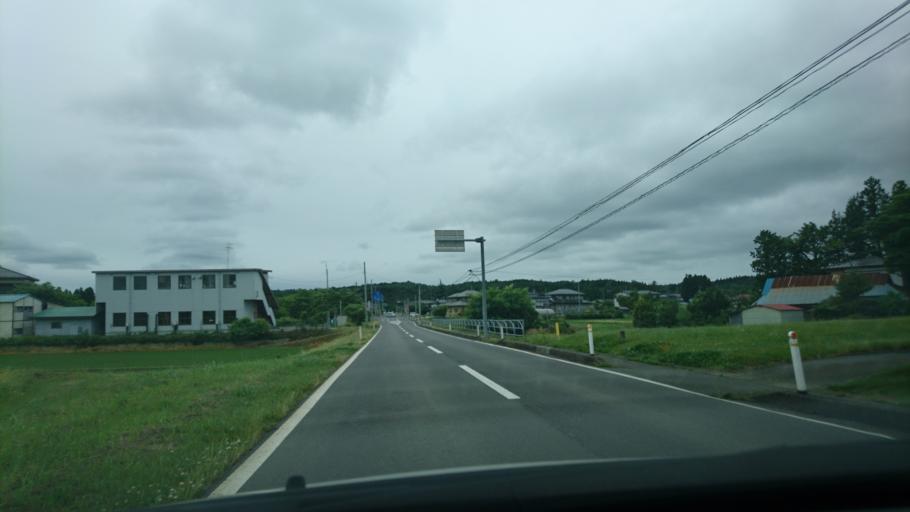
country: JP
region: Iwate
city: Ichinoseki
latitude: 38.9483
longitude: 141.0509
